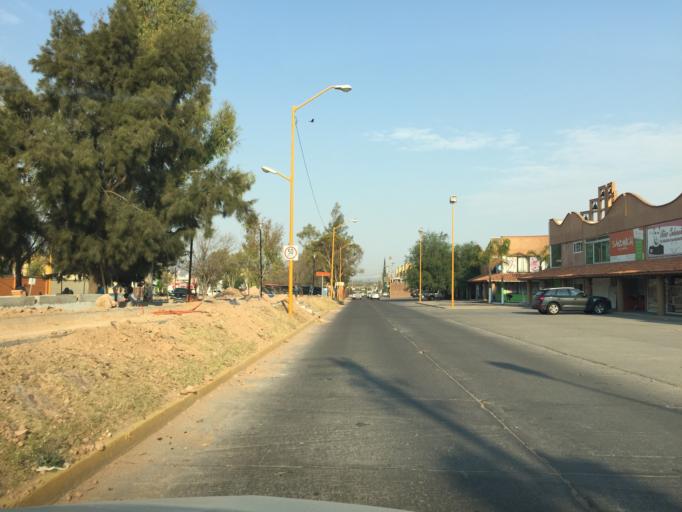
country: MX
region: Aguascalientes
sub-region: Aguascalientes
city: Pocitos
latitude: 21.9029
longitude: -102.3111
